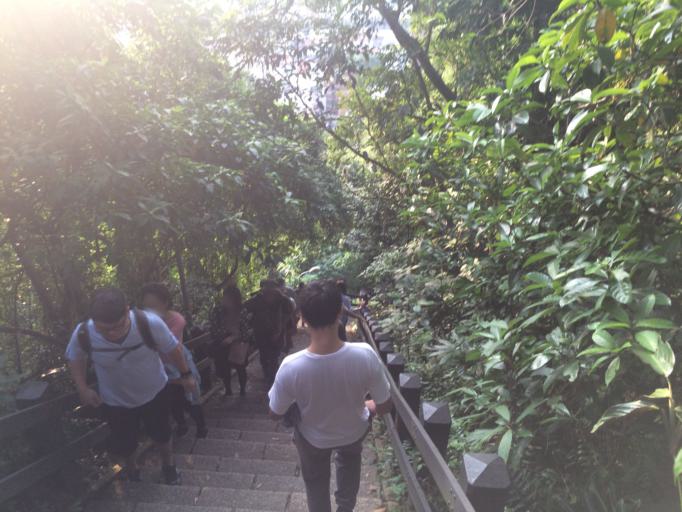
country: TW
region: Taipei
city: Taipei
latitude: 25.0272
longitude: 121.5723
